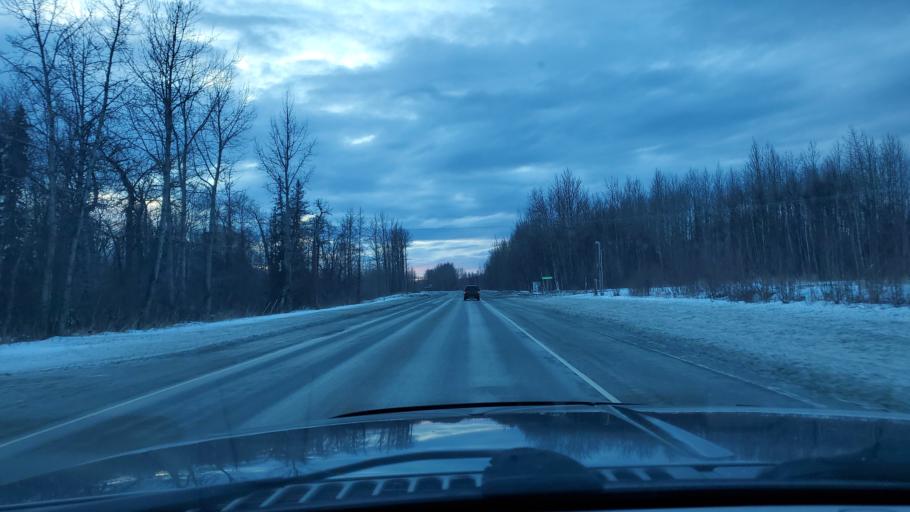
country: US
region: Alaska
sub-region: Matanuska-Susitna Borough
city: Farm Loop
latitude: 61.6643
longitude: -149.0862
